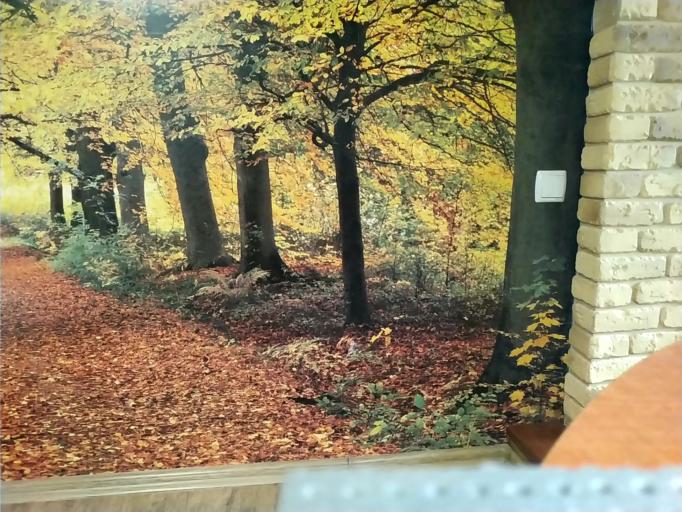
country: RU
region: Tverskaya
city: Kalashnikovo
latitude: 57.2661
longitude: 35.1546
